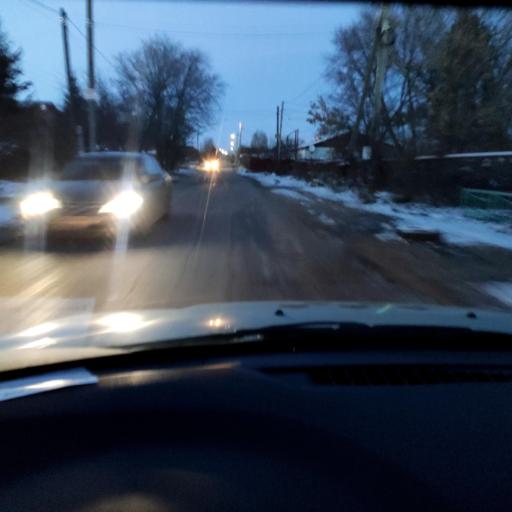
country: RU
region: Samara
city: Tol'yatti
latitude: 53.5642
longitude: 49.3897
